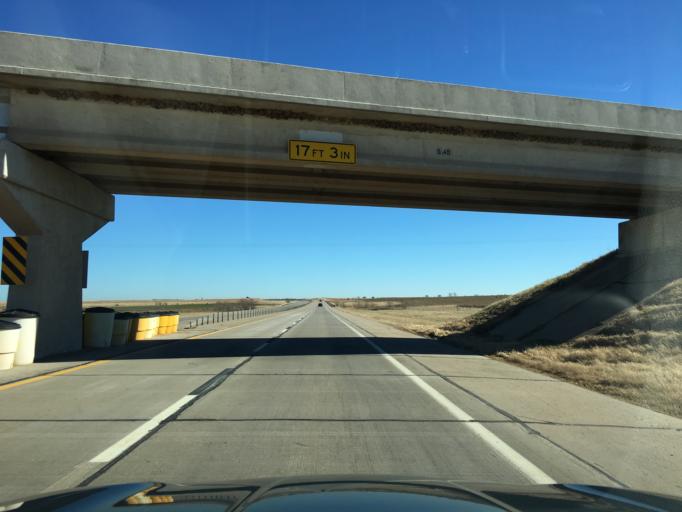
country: US
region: Oklahoma
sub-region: Noble County
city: Perry
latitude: 36.3968
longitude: -97.2296
